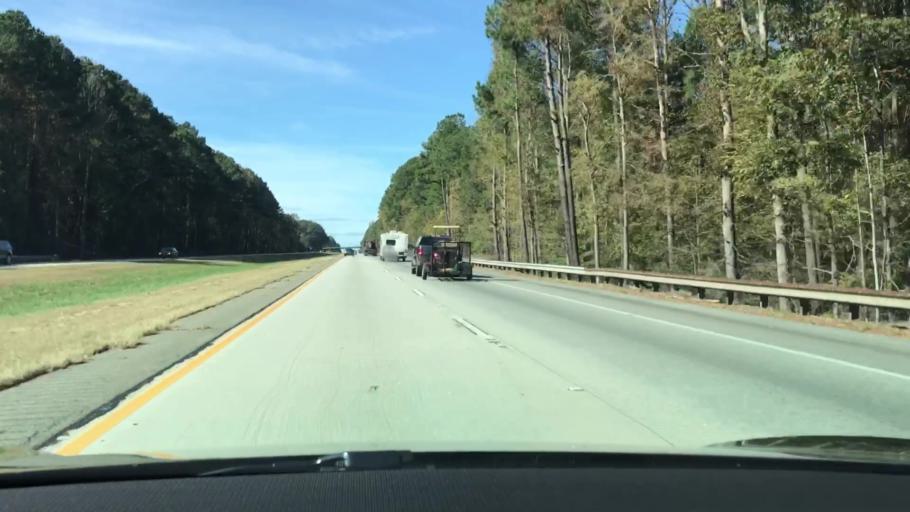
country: US
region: Georgia
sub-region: Greene County
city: Greensboro
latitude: 33.5485
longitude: -83.1557
